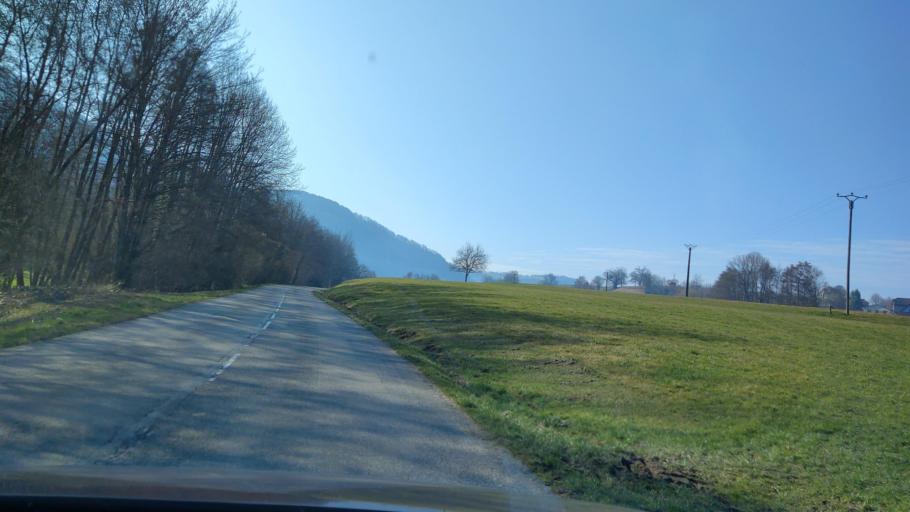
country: FR
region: Rhone-Alpes
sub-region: Departement de la Savoie
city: La Bridoire
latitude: 45.5142
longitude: 5.7372
